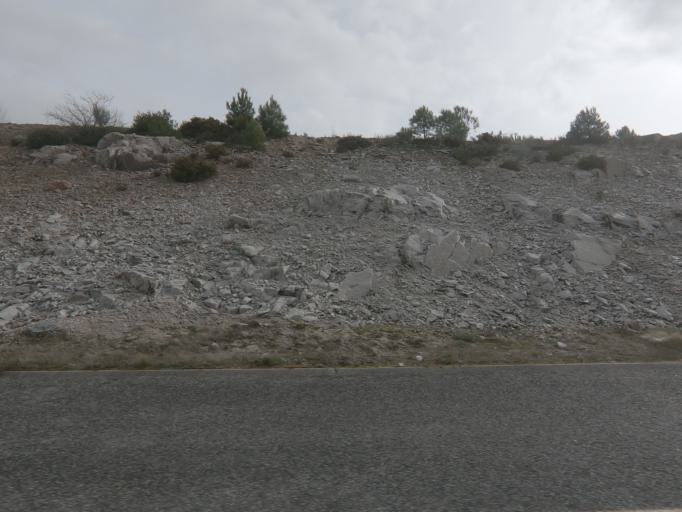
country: PT
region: Vila Real
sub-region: Vila Pouca de Aguiar
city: Vila Pouca de Aguiar
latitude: 41.5341
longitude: -7.6325
